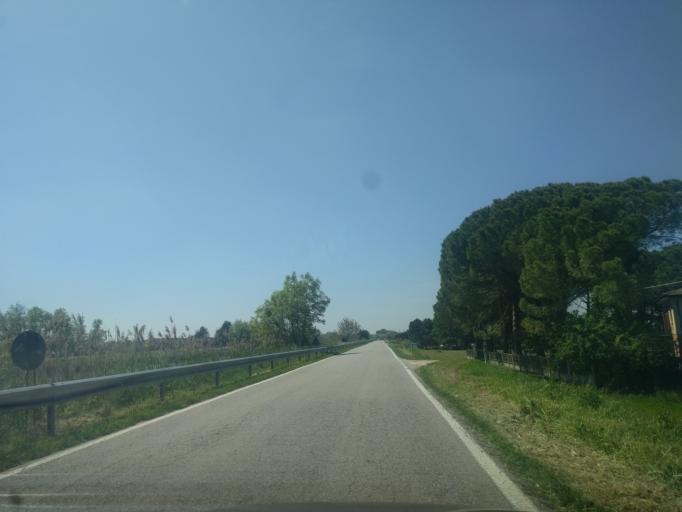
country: IT
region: Veneto
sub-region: Provincia di Rovigo
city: Villanova Marchesana
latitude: 45.0472
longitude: 11.9814
